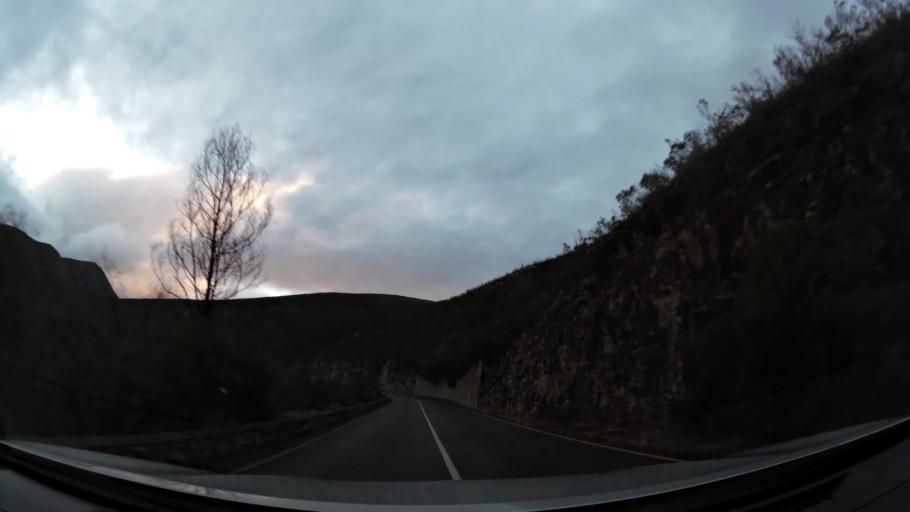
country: ZA
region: Western Cape
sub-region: Overberg District Municipality
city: Swellendam
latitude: -33.9813
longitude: 20.7097
